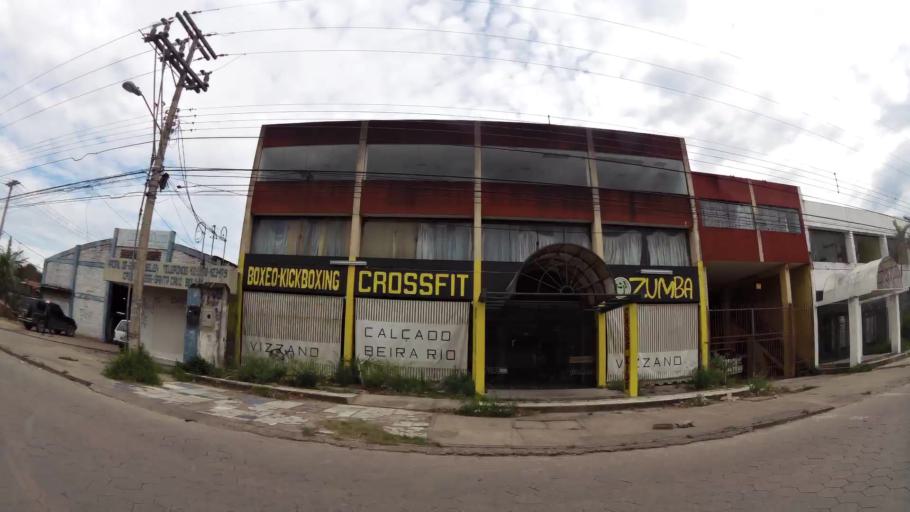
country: BO
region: Santa Cruz
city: Santa Cruz de la Sierra
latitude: -17.7572
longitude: -63.1881
